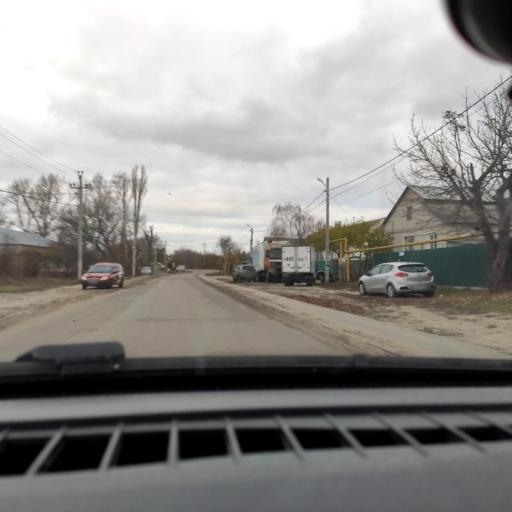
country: RU
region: Voronezj
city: Podgornoye
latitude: 51.7335
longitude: 39.1394
